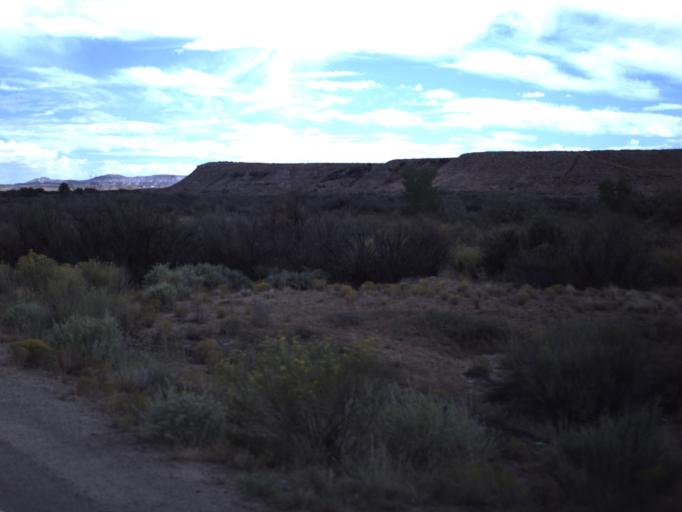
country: US
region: Utah
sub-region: San Juan County
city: Blanding
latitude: 37.2729
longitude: -109.3304
